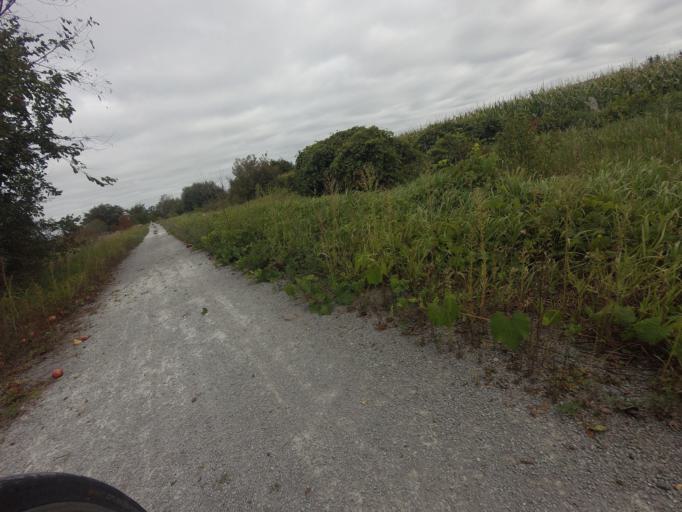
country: CA
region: Ontario
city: Omemee
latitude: 44.3157
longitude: -78.8575
